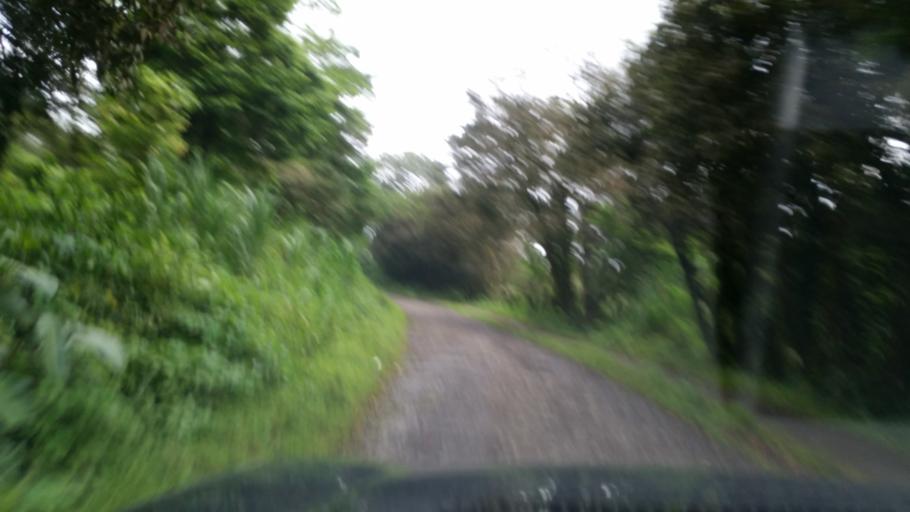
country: NI
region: Jinotega
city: San Jose de Bocay
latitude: 13.2801
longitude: -85.7168
